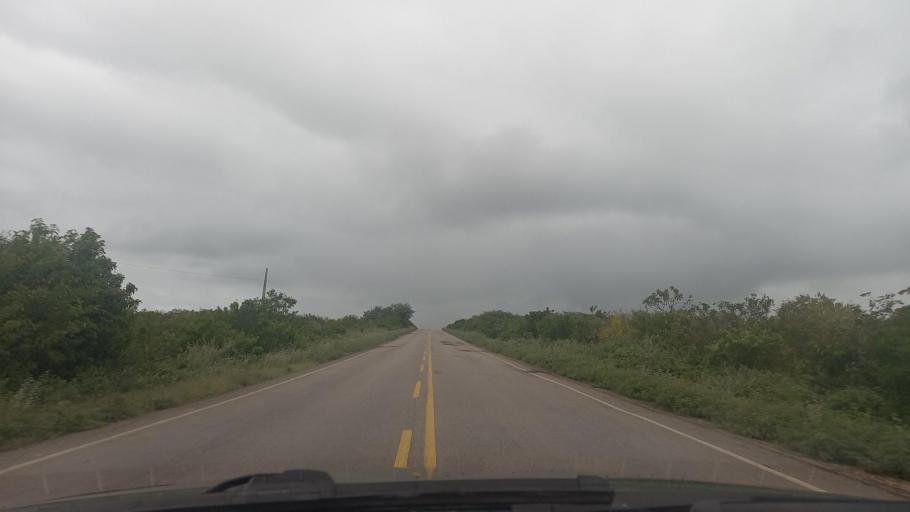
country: BR
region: Bahia
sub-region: Paulo Afonso
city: Paulo Afonso
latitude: -9.3270
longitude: -38.2878
